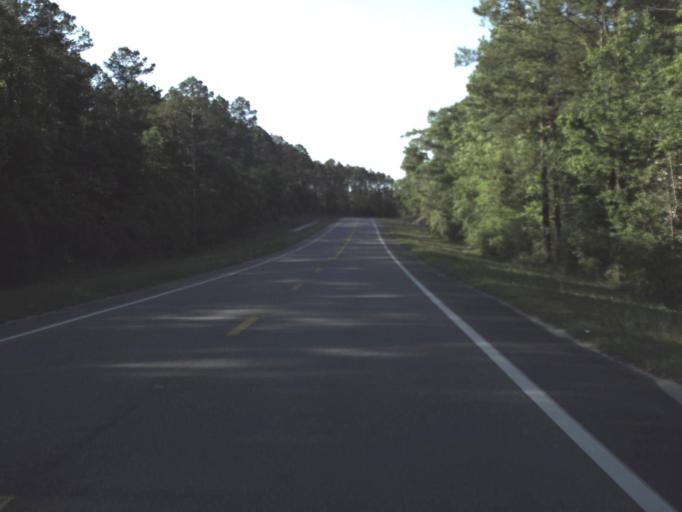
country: US
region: Florida
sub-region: Liberty County
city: Bristol
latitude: 30.4116
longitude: -84.7845
